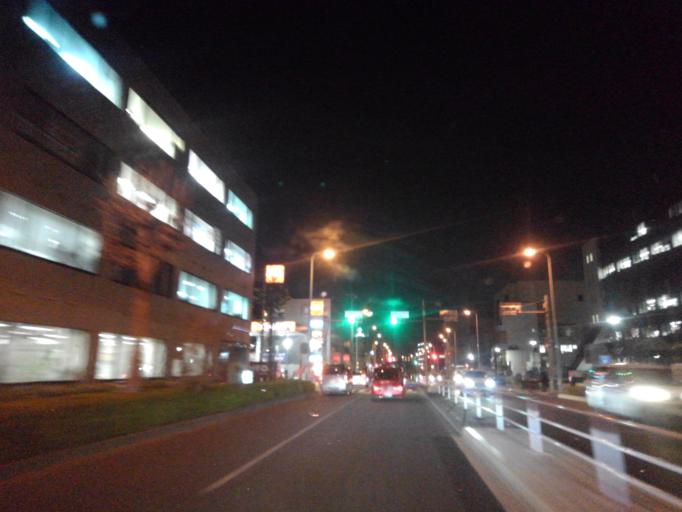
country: JP
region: Tokyo
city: Chofugaoka
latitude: 35.6385
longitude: 139.5040
